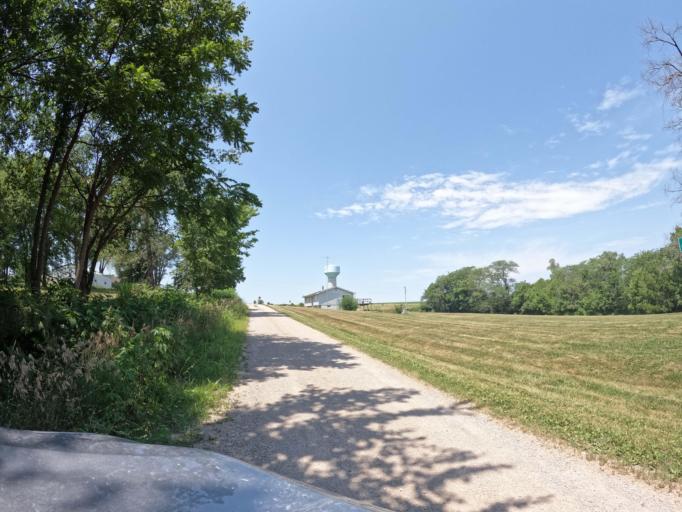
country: US
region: Iowa
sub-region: Appanoose County
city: Centerville
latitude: 40.7862
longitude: -92.9049
